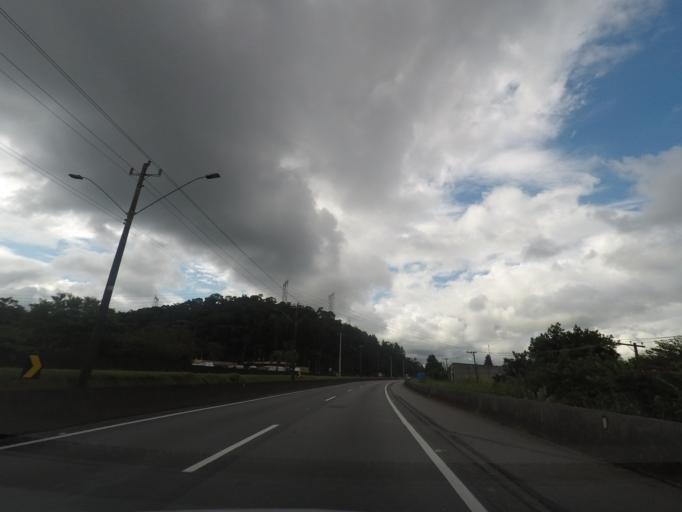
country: BR
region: Sao Paulo
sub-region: Sao Lourenco Da Serra
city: Sao Lourenco da Serra
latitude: -23.8923
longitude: -46.9835
